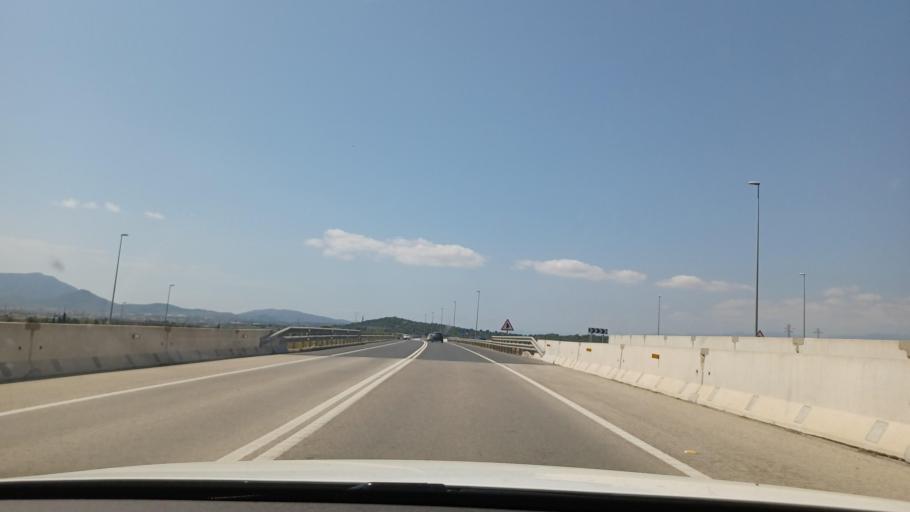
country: ES
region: Catalonia
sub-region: Provincia de Tarragona
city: Amposta
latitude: 40.7529
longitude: 0.6059
